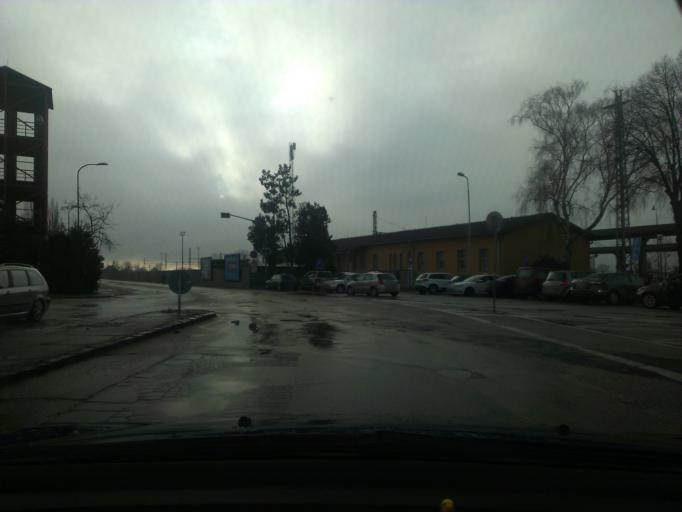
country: SK
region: Trnavsky
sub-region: Okres Trnava
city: Piestany
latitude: 48.5958
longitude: 17.8152
